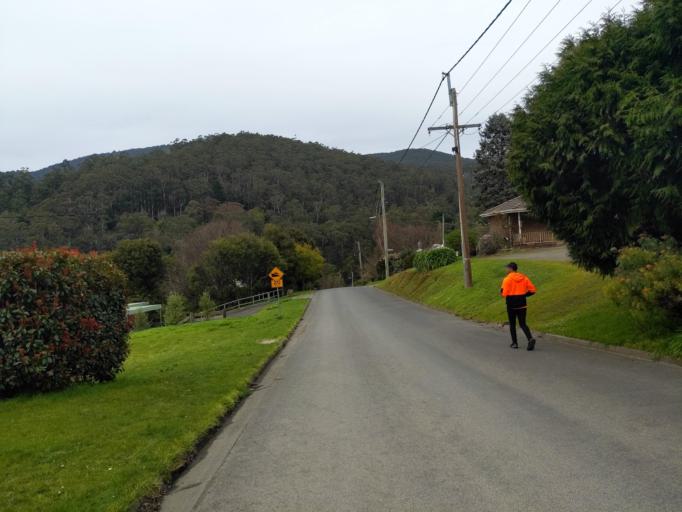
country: AU
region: Victoria
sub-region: Yarra Ranges
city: Millgrove
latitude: -37.7503
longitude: 145.6929
